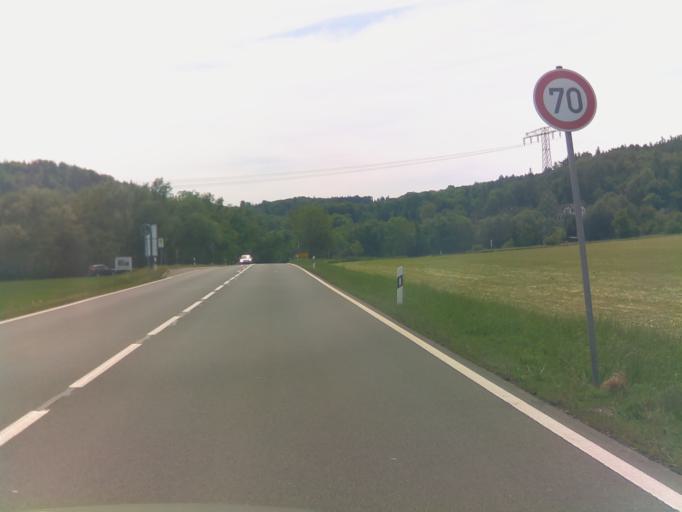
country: DE
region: Saxony-Anhalt
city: Blankenburg
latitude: 51.7650
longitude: 10.9614
